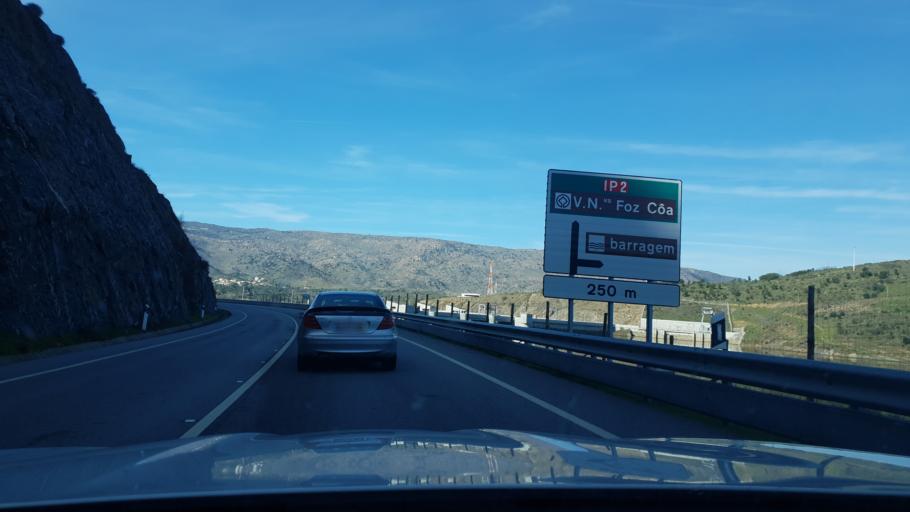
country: PT
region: Braganca
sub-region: Torre de Moncorvo
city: Torre de Moncorvo
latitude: 41.2013
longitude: -7.0892
